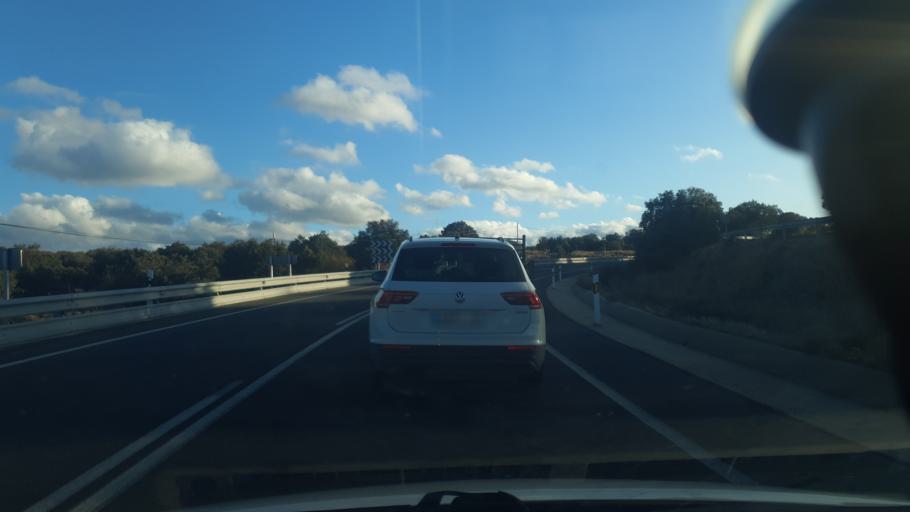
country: ES
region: Castille and Leon
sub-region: Provincia de Avila
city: Mingorria
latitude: 40.7205
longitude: -4.6730
